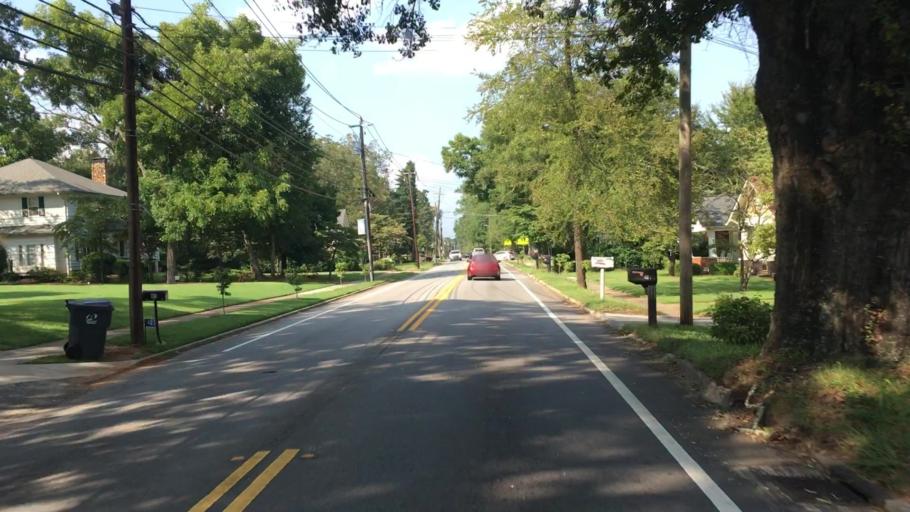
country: US
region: Georgia
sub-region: Walton County
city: Social Circle
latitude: 33.6607
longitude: -83.7155
